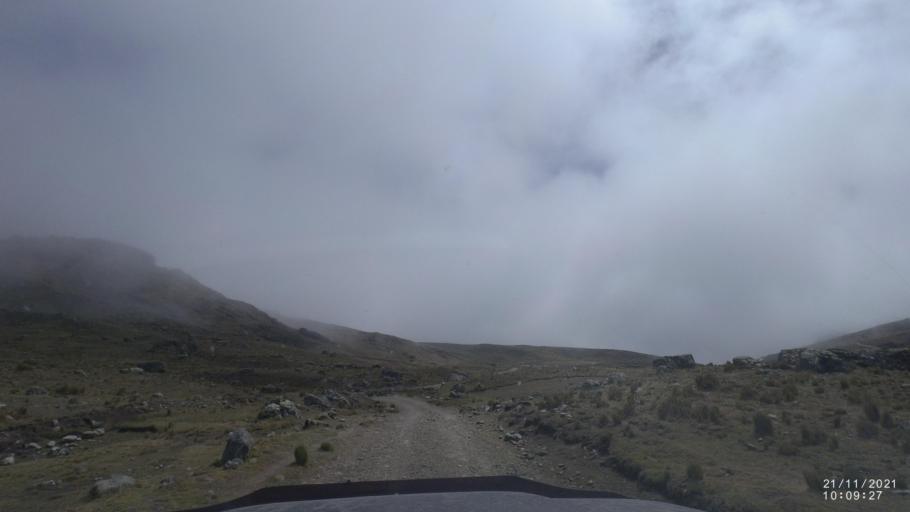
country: BO
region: Cochabamba
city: Cochabamba
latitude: -16.9989
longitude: -66.2774
